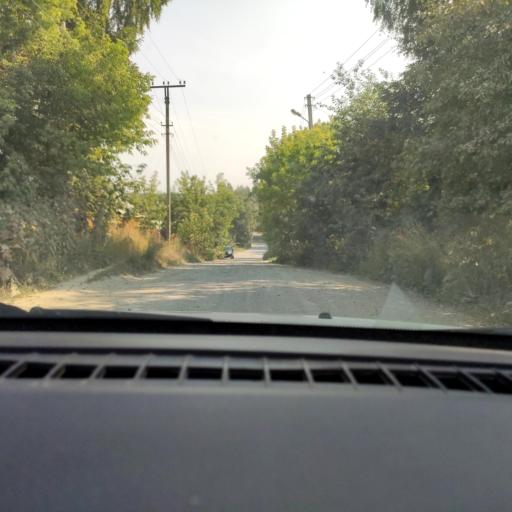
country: RU
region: Perm
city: Polazna
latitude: 58.1432
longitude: 56.4567
